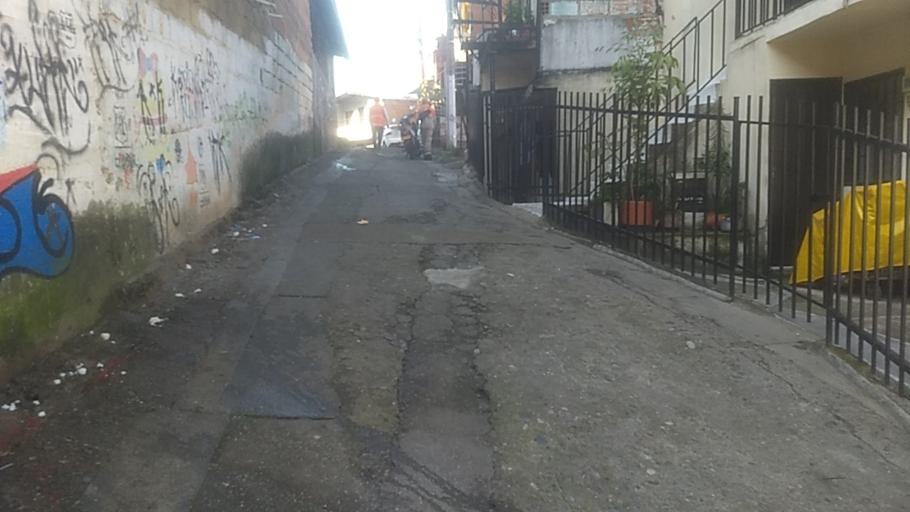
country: CO
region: Antioquia
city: Bello
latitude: 6.2984
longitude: -75.5476
